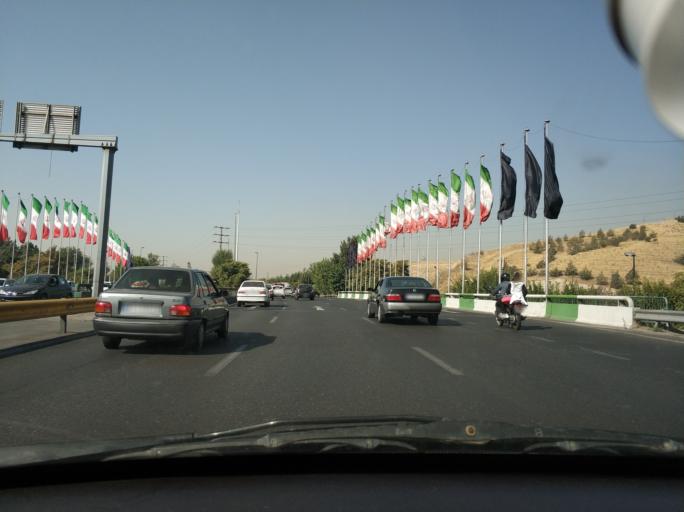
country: IR
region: Tehran
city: Tehran
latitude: 35.7427
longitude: 51.4362
